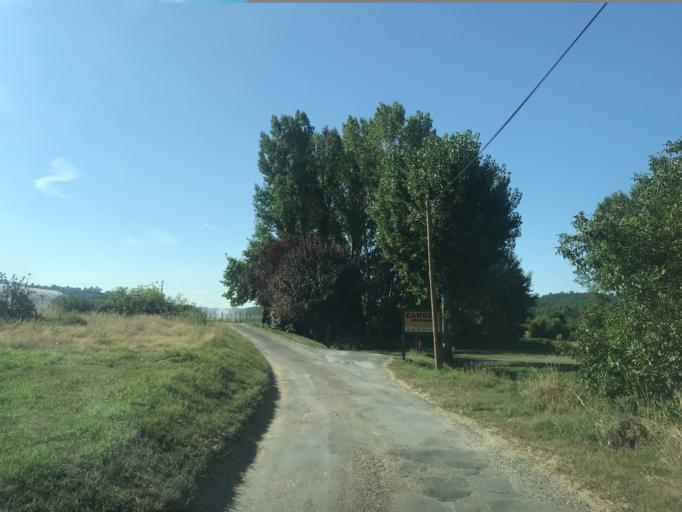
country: FR
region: Aquitaine
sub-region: Departement de la Dordogne
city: Cenac-et-Saint-Julien
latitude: 44.8163
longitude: 1.1856
